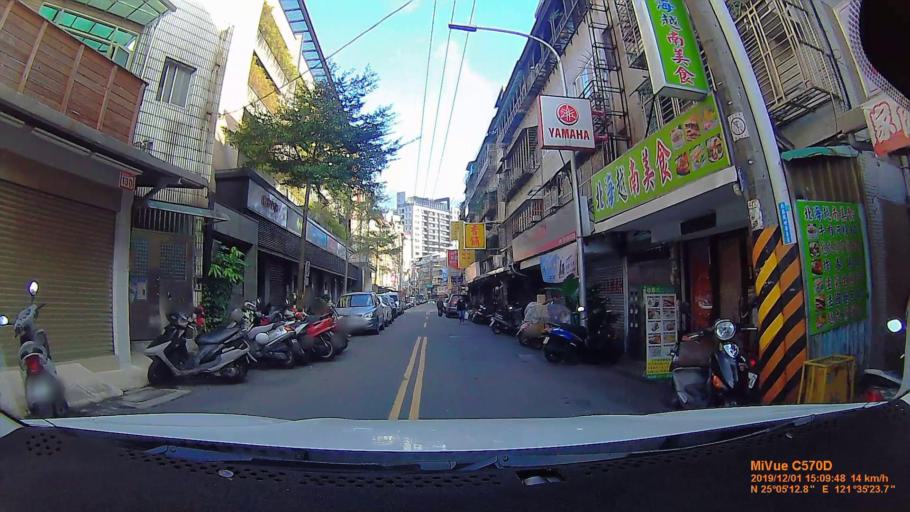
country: TW
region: Taipei
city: Taipei
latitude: 25.0868
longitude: 121.5901
